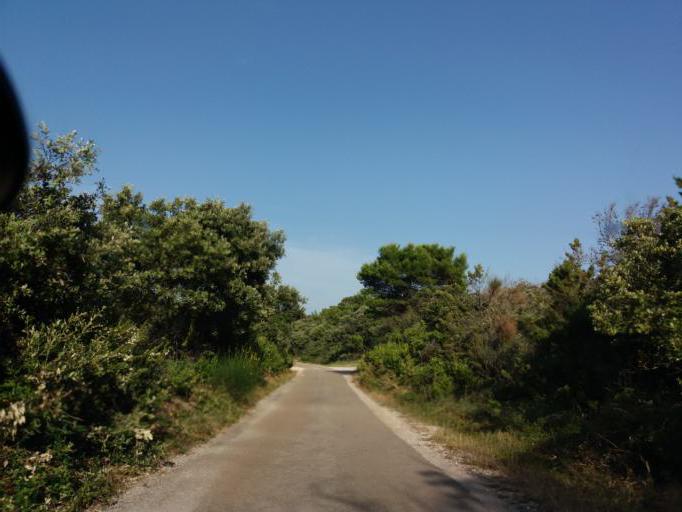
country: HR
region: Zadarska
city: Ugljan
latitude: 44.1457
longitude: 14.8349
